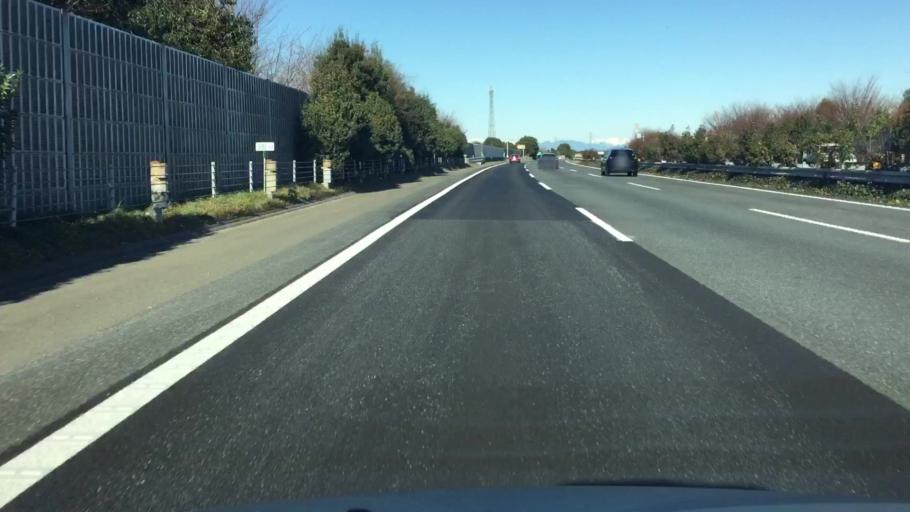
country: JP
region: Saitama
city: Yorii
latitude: 36.1396
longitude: 139.2262
